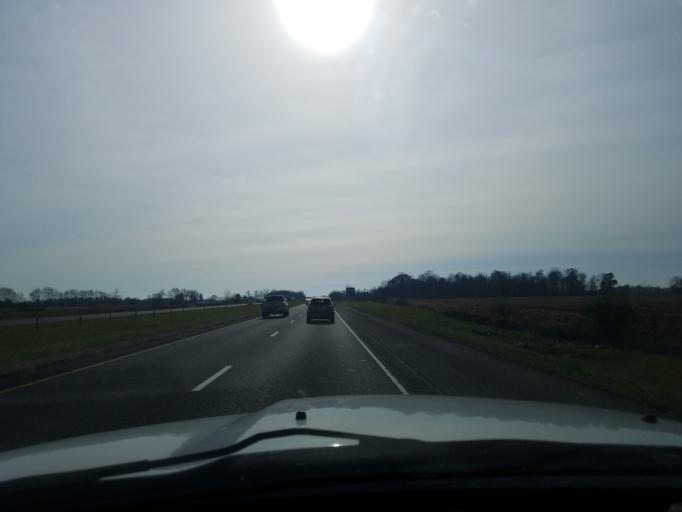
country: US
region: Indiana
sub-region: Delaware County
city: Daleville
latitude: 40.1431
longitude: -85.5675
